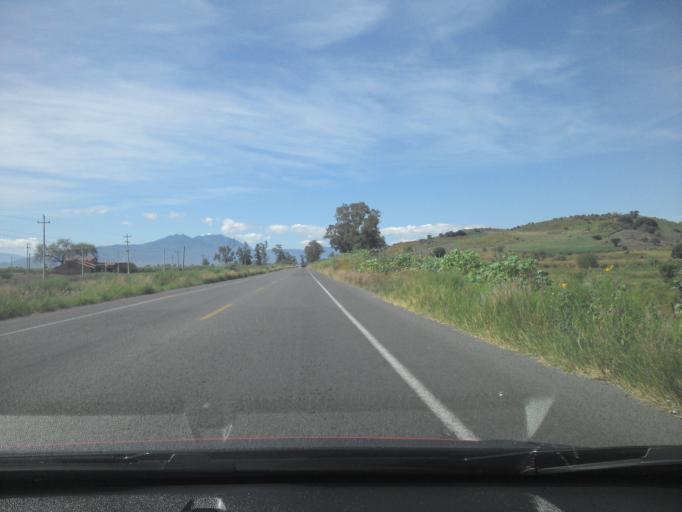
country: MX
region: Jalisco
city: El Refugio
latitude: 20.6660
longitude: -103.7666
